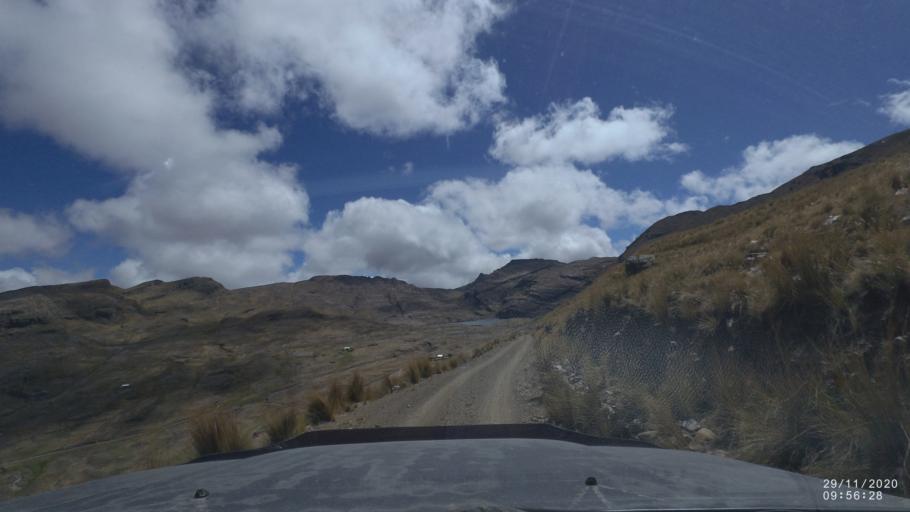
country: BO
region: Cochabamba
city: Cochabamba
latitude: -17.2714
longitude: -66.1740
